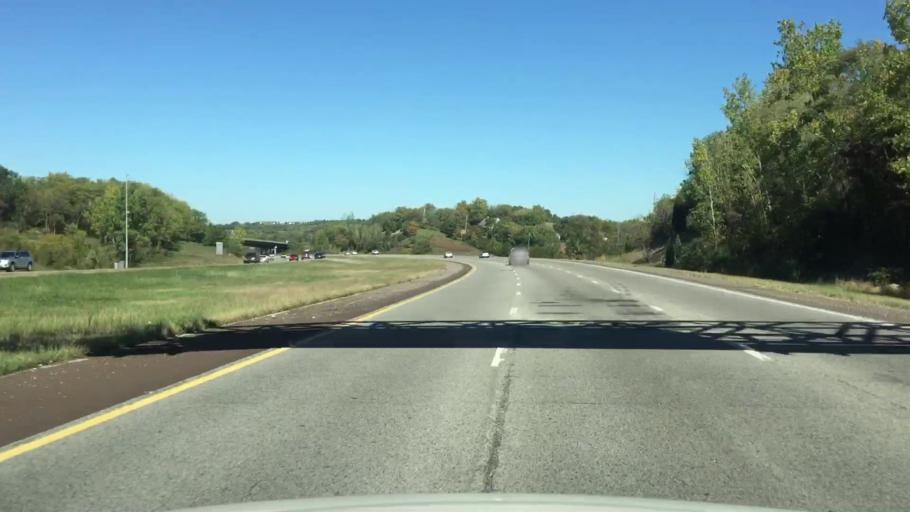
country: US
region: Kansas
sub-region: Johnson County
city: Lenexa
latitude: 38.9880
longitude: -94.7760
